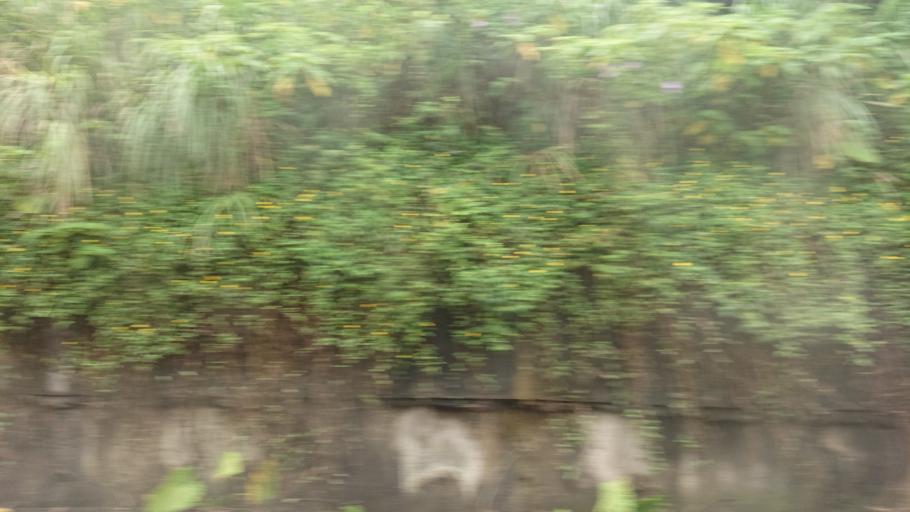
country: TW
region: Taiwan
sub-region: Keelung
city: Keelung
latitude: 25.0791
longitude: 121.6983
